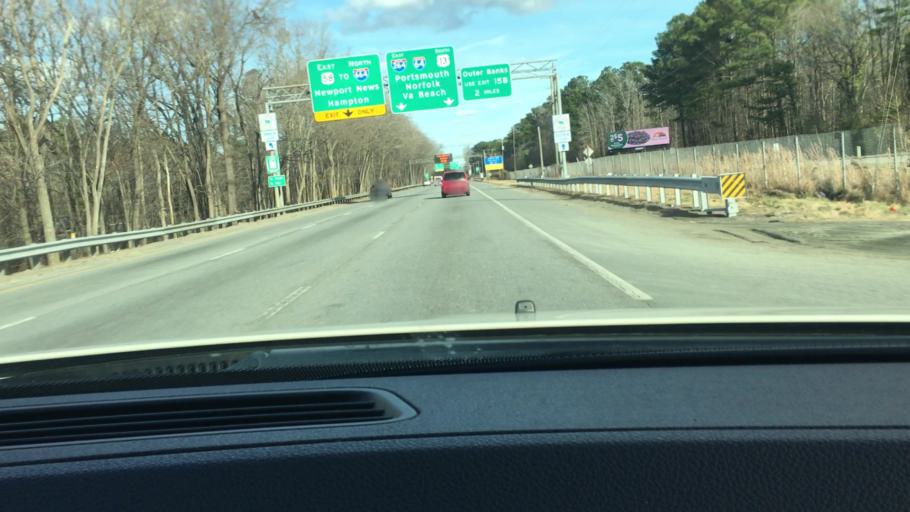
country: US
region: Virginia
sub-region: City of Portsmouth
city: Portsmouth Heights
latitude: 36.7785
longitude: -76.4379
